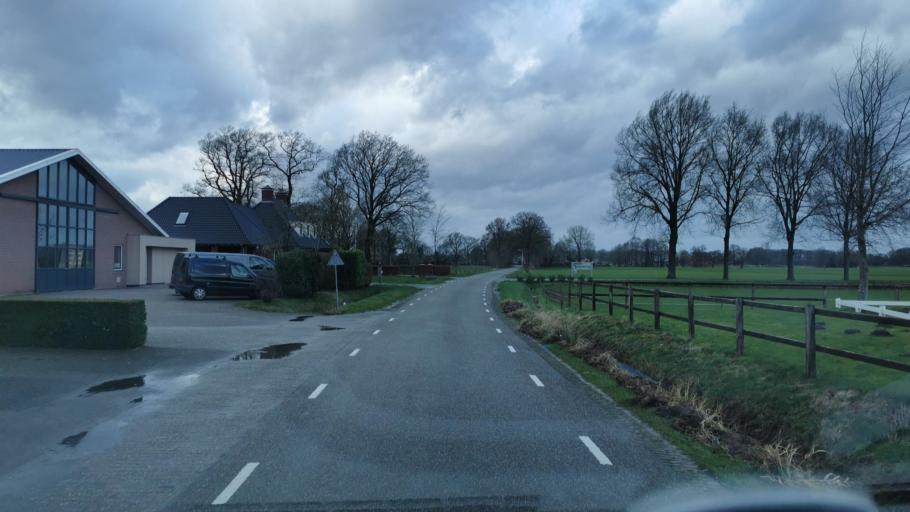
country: DE
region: Lower Saxony
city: Lage
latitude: 52.4197
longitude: 6.9863
